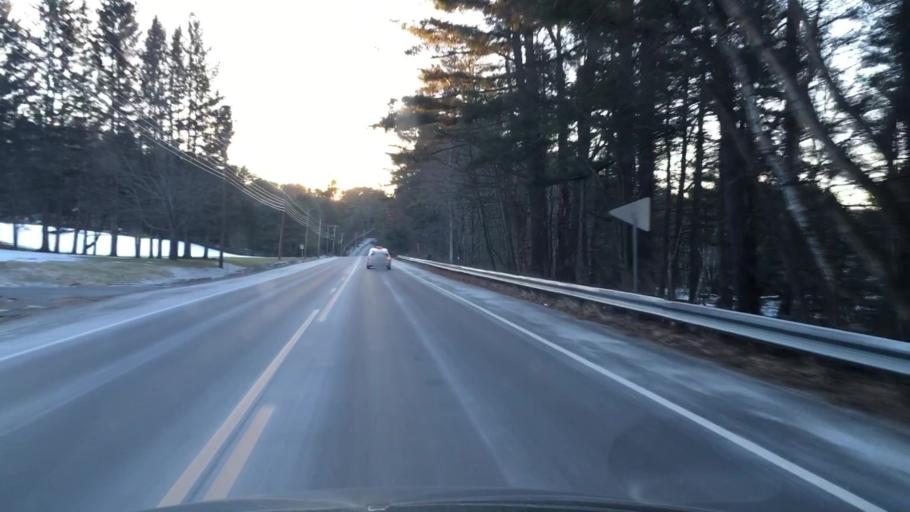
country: US
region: New Hampshire
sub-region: Grafton County
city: Hanover
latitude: 43.7348
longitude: -72.2548
